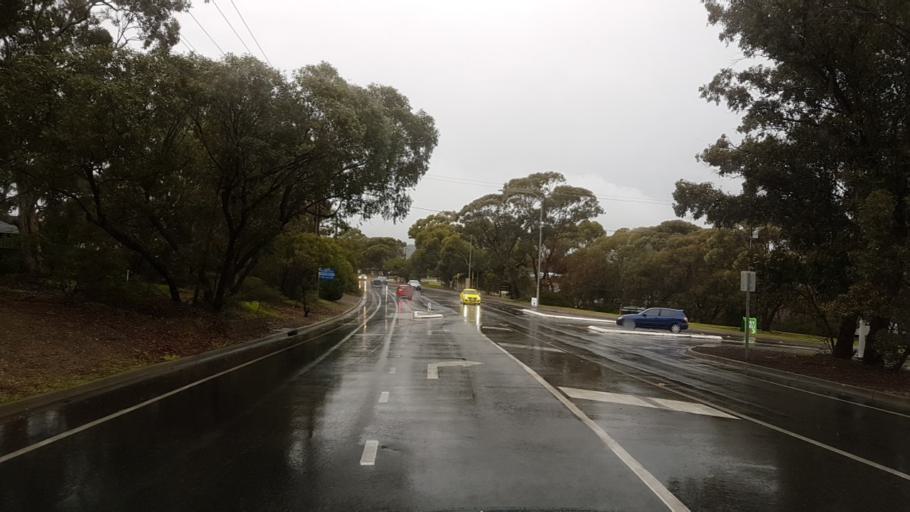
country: AU
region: South Australia
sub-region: Onkaparinga
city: Craigburn Farm
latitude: -35.0577
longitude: 138.6015
